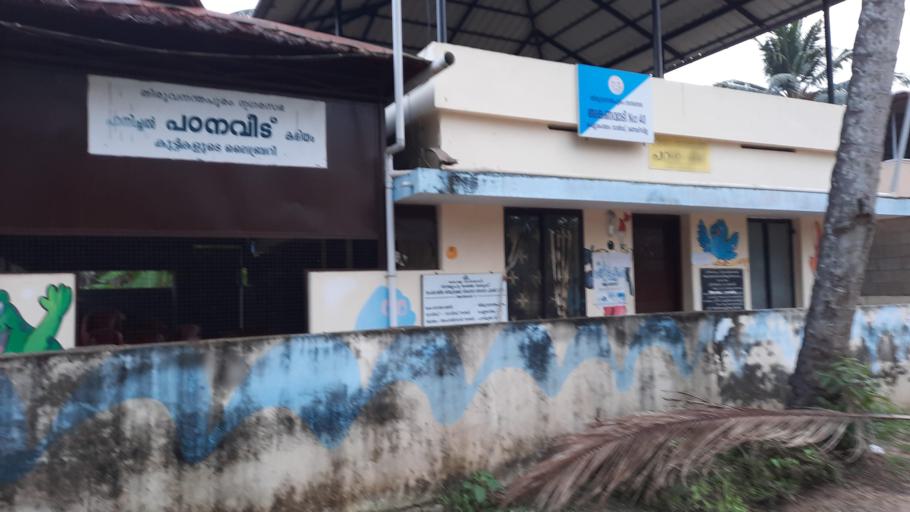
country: IN
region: Kerala
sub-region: Thiruvananthapuram
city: Thiruvananthapuram
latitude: 8.5590
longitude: 76.9272
